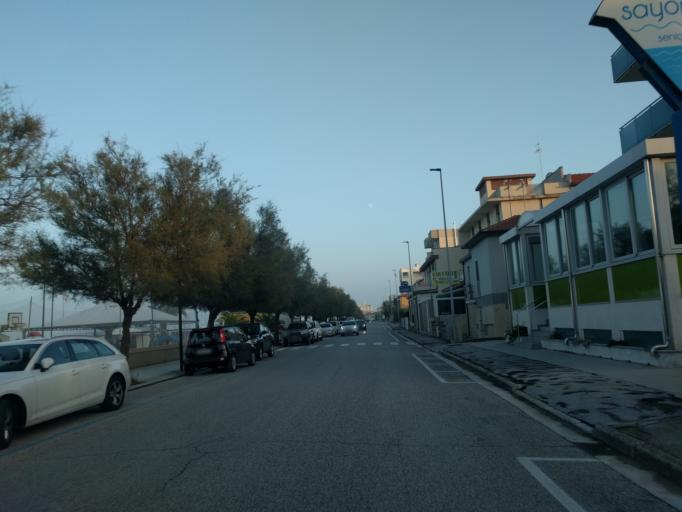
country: IT
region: The Marches
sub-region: Provincia di Ancona
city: Senigallia
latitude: 43.7270
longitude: 13.2063
